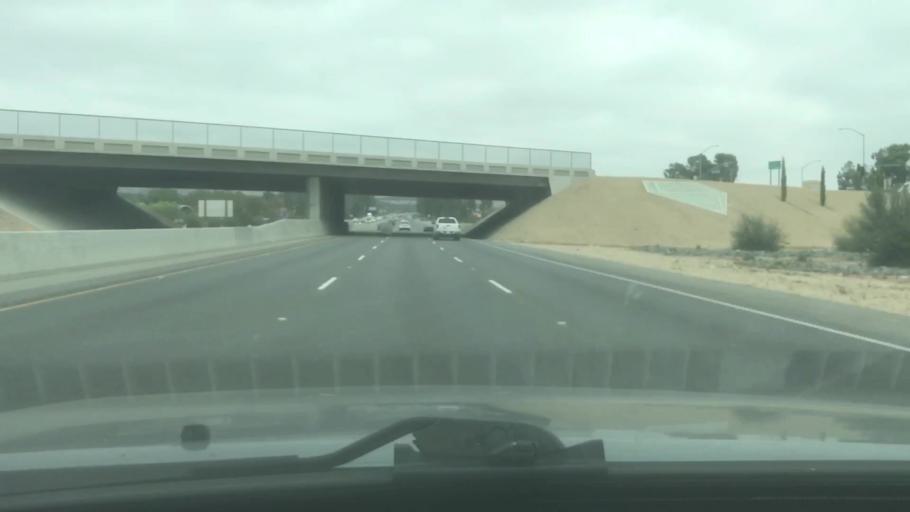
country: US
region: California
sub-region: Riverside County
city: Murrieta Hot Springs
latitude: 33.5720
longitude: -117.1808
